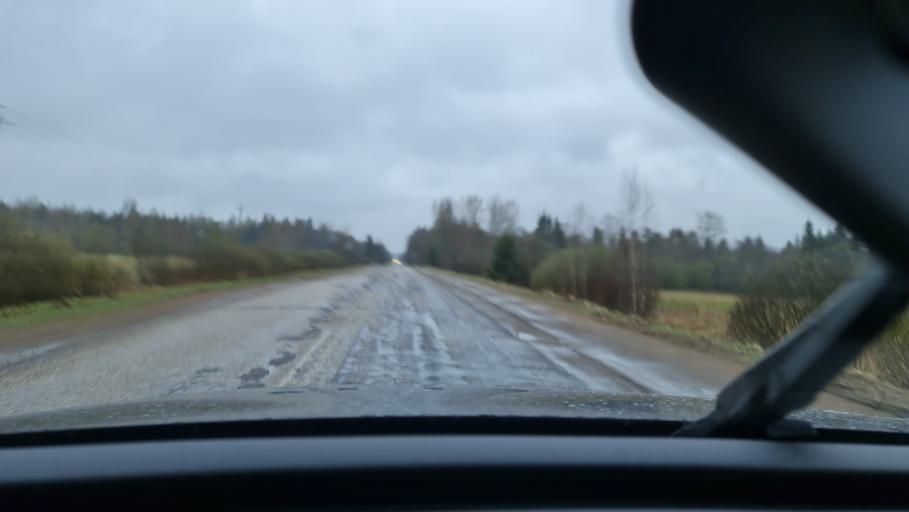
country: RU
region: Novgorod
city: Valday
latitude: 58.0357
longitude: 32.8787
